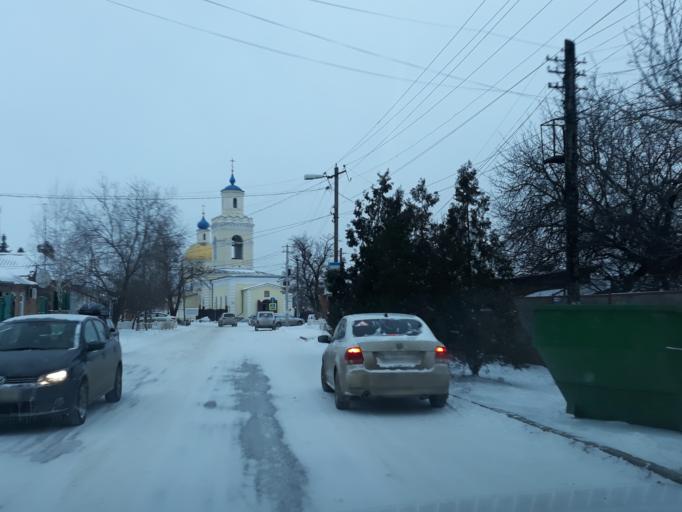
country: RU
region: Rostov
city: Taganrog
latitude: 47.2014
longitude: 38.9385
